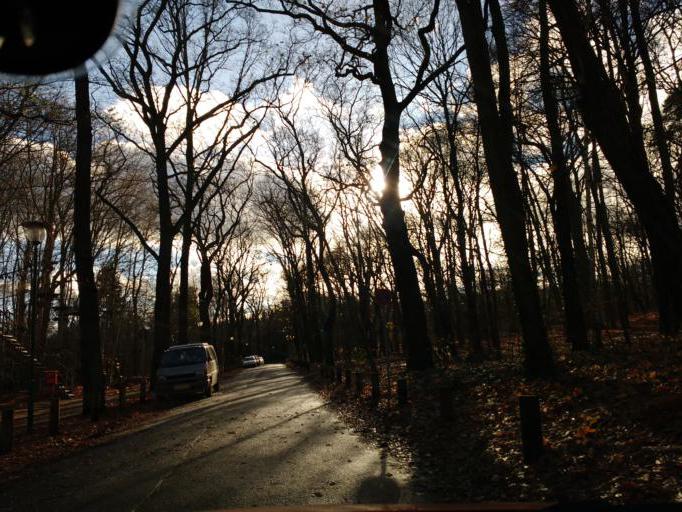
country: DE
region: Brandenburg
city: Potsdam
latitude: 52.3846
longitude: 13.0669
